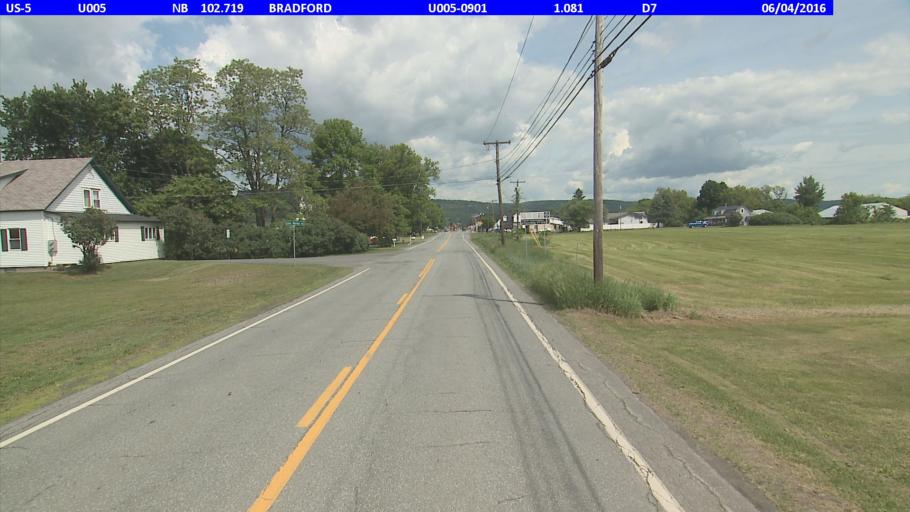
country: US
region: New Hampshire
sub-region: Grafton County
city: Orford
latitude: 43.9767
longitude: -72.1185
